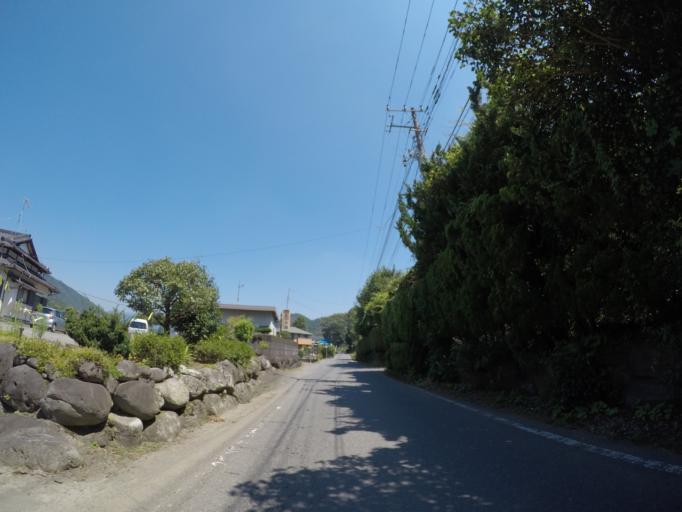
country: JP
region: Shizuoka
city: Fujinomiya
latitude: 35.2166
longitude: 138.5661
